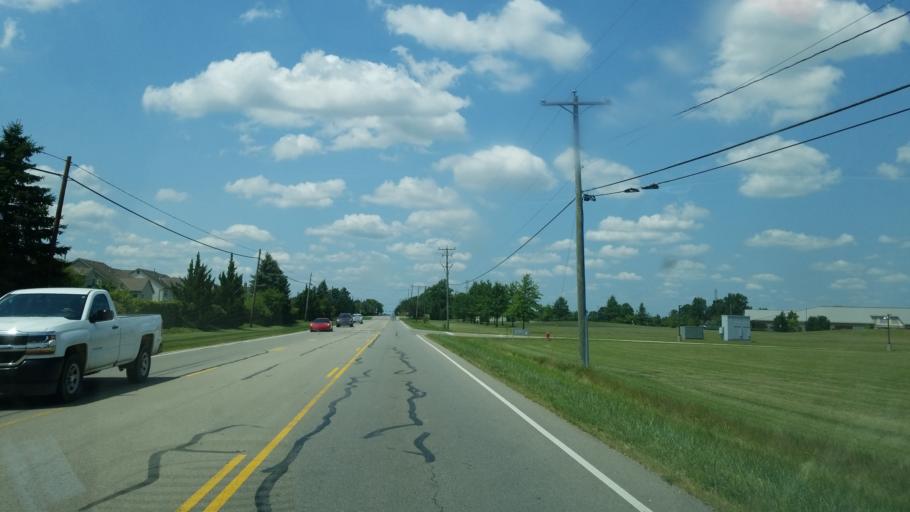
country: US
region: Ohio
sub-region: Delaware County
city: Powell
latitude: 40.1960
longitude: -83.0995
